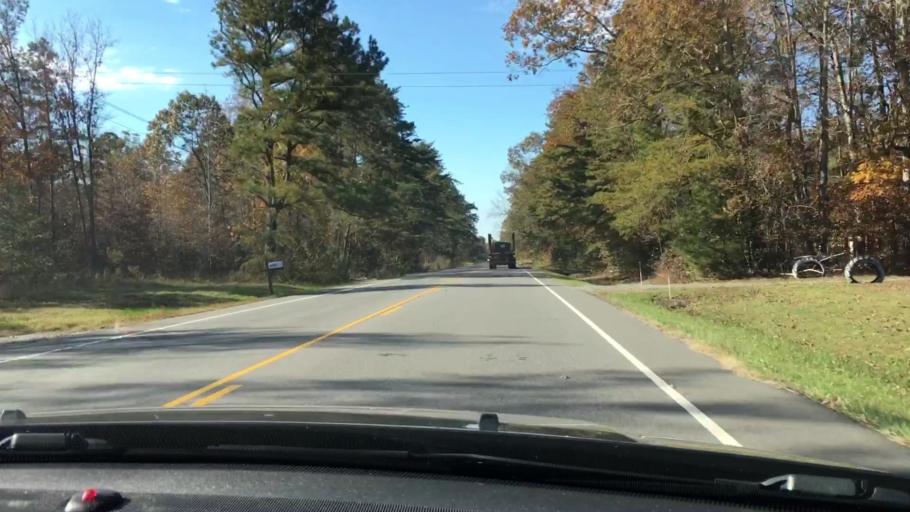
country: US
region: Virginia
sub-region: Hanover County
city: Hanover
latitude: 37.7958
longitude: -77.2482
